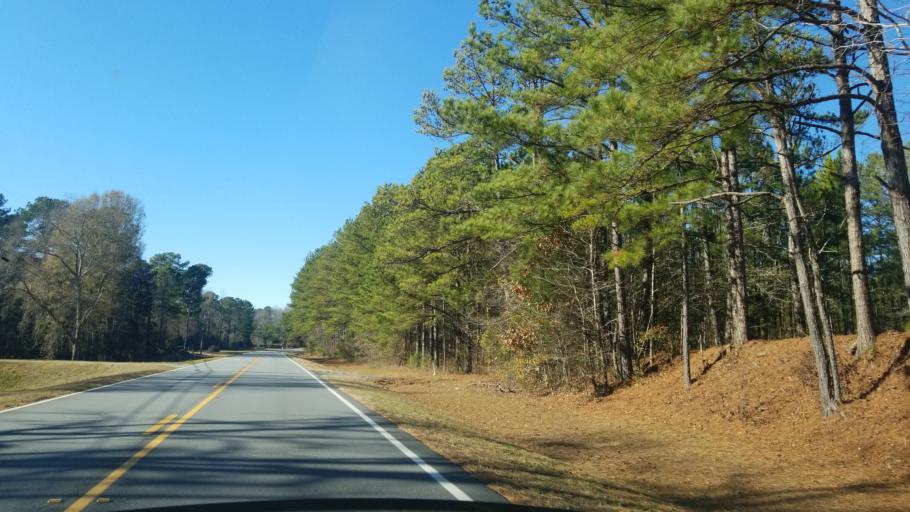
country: US
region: Georgia
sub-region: Harris County
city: Hamilton
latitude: 32.6696
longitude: -84.9005
